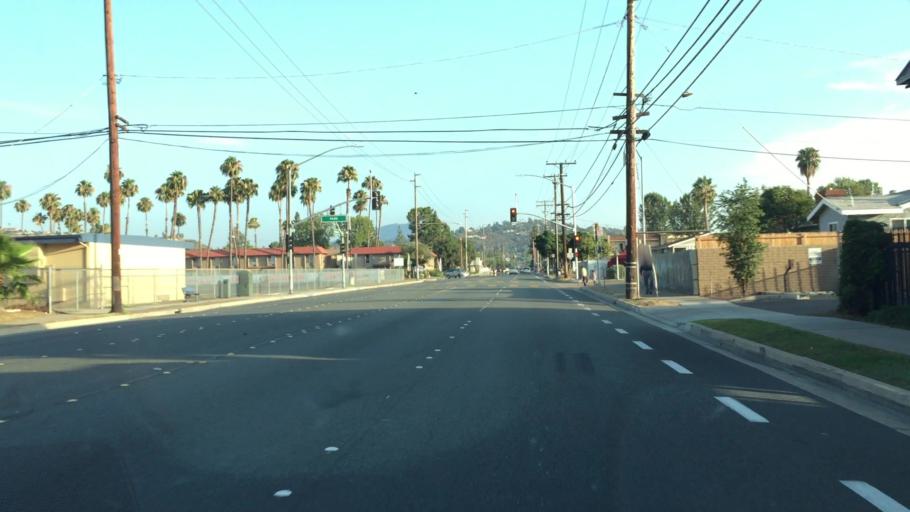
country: US
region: California
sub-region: San Diego County
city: El Cajon
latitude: 32.7988
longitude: -116.9511
